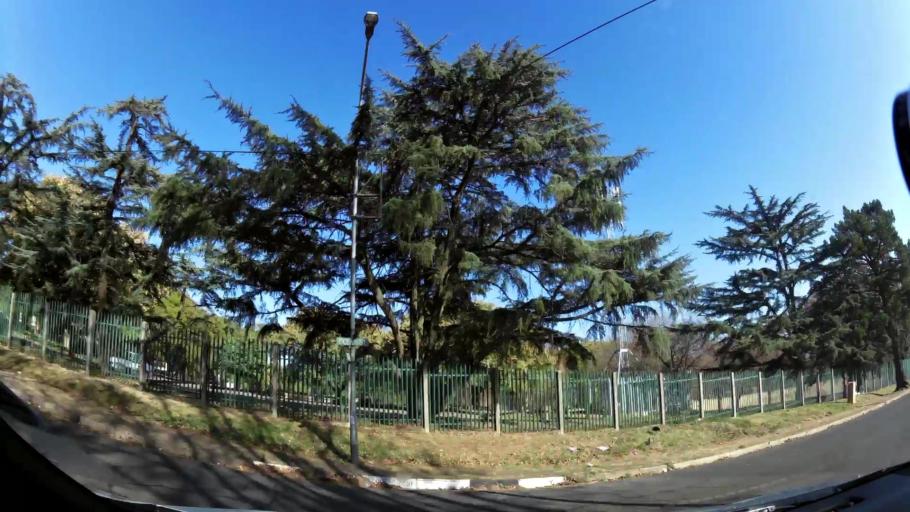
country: ZA
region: Gauteng
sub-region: City of Johannesburg Metropolitan Municipality
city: Johannesburg
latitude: -26.1907
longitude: 28.1002
